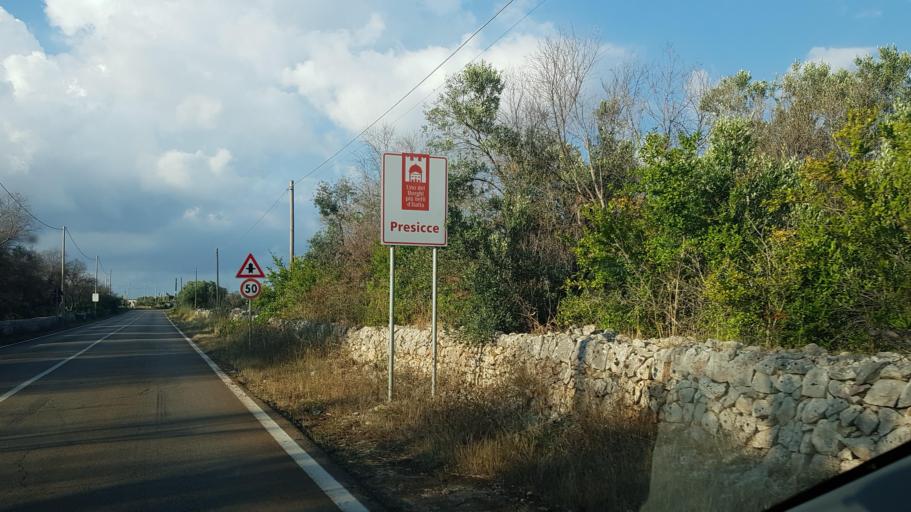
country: IT
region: Apulia
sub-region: Provincia di Lecce
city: Gemini
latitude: 39.8619
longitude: 18.2068
